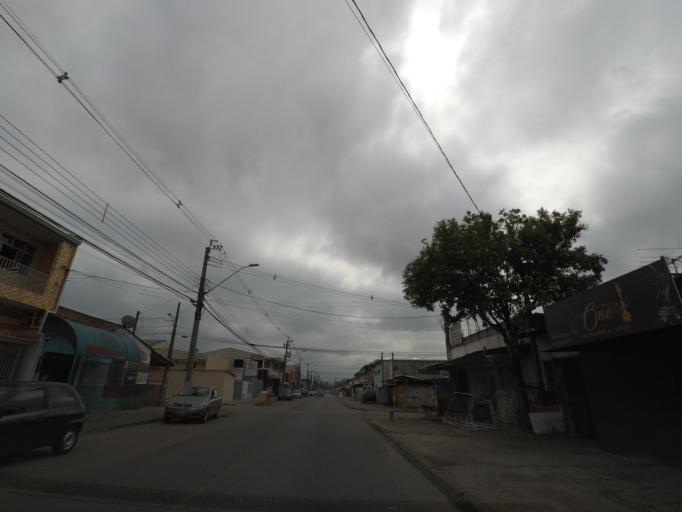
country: BR
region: Parana
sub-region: Curitiba
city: Curitiba
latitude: -25.5053
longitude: -49.3379
